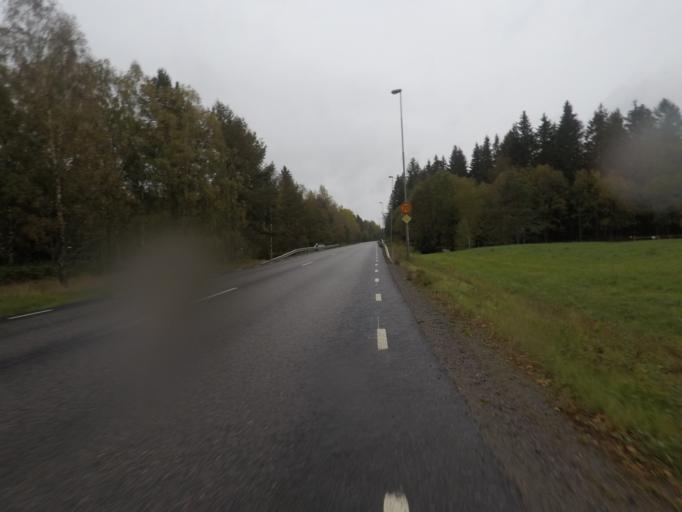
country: SE
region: OErebro
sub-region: Karlskoga Kommun
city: Karlskoga
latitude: 59.3122
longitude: 14.4690
